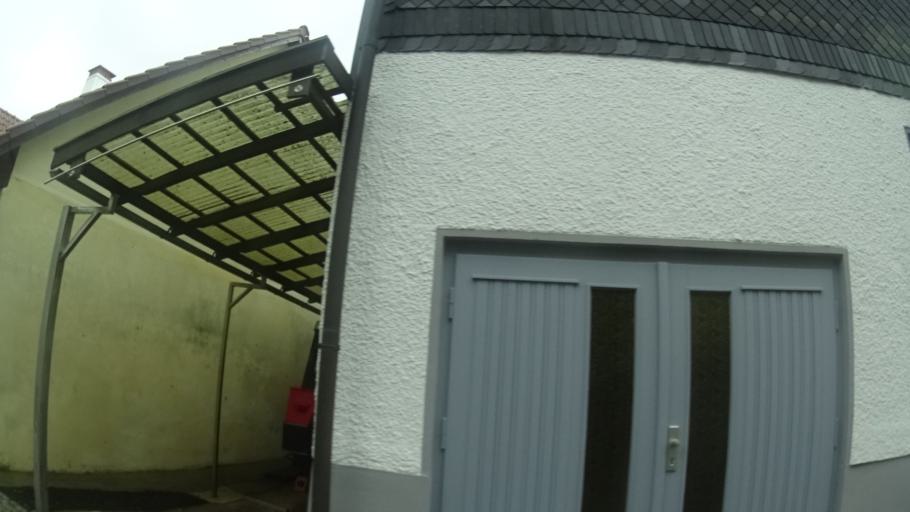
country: DE
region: Thuringia
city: Eisfeld
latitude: 50.4873
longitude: 10.8517
